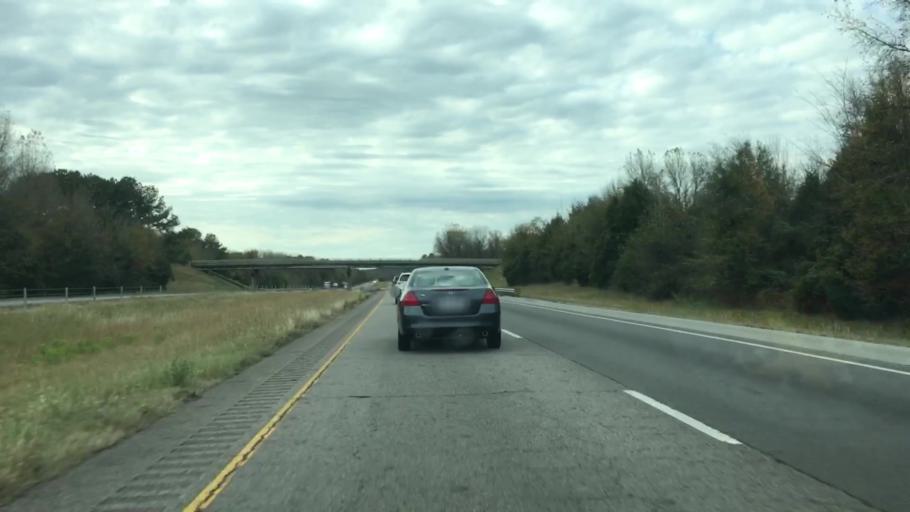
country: US
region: Arkansas
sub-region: Faulkner County
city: Conway
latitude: 35.1527
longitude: -92.5514
